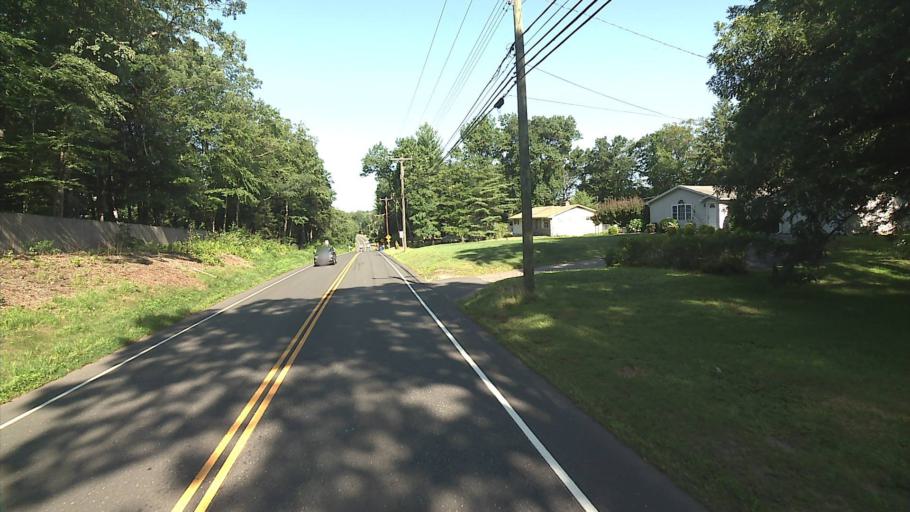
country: US
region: Connecticut
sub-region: Hartford County
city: Salmon Brook
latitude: 41.9511
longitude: -72.7562
